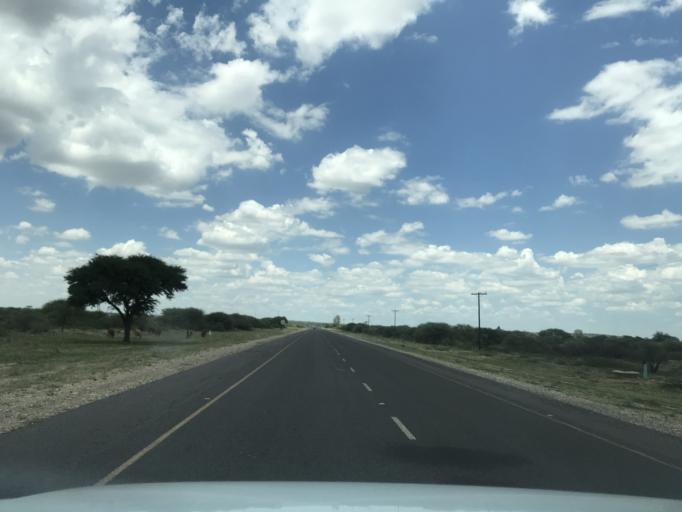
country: BW
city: Mabuli
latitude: -25.7287
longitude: 25.1121
